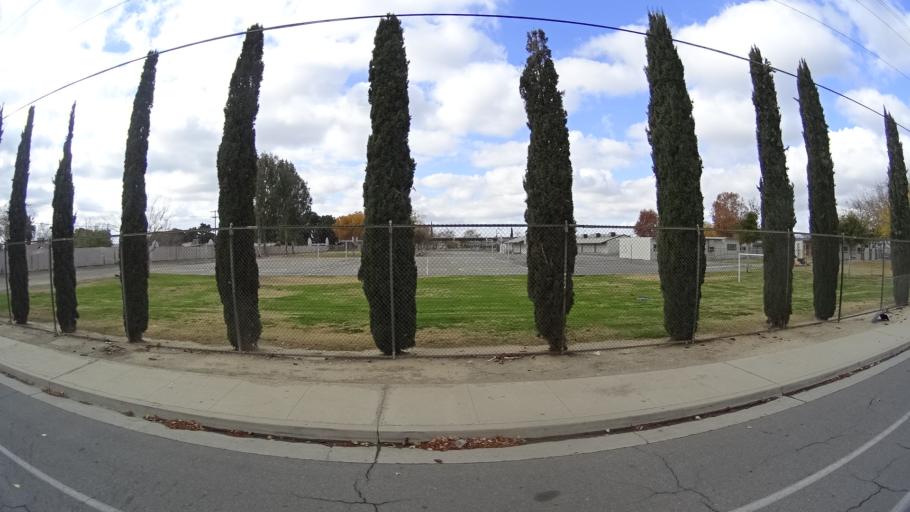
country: US
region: California
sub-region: Kern County
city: Bakersfield
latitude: 35.3637
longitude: -118.9676
